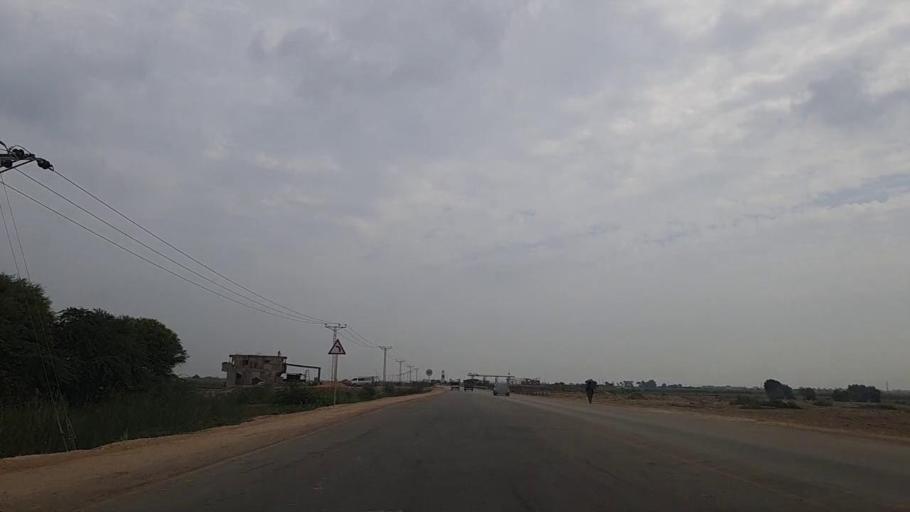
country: PK
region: Sindh
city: Thatta
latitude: 24.6153
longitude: 68.0557
